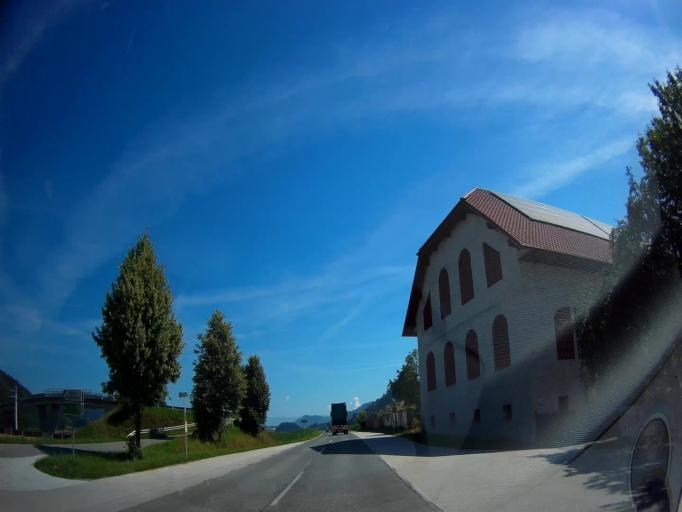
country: AT
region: Carinthia
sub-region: Politischer Bezirk Klagenfurt Land
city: Maria Saal
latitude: 46.7029
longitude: 14.3601
